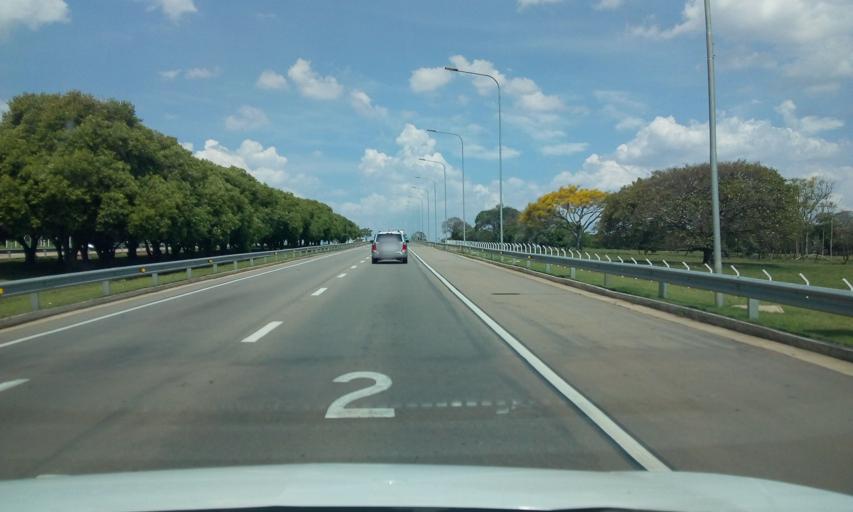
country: BR
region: Sao Paulo
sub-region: Indaiatuba
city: Indaiatuba
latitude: -23.0194
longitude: -47.1341
